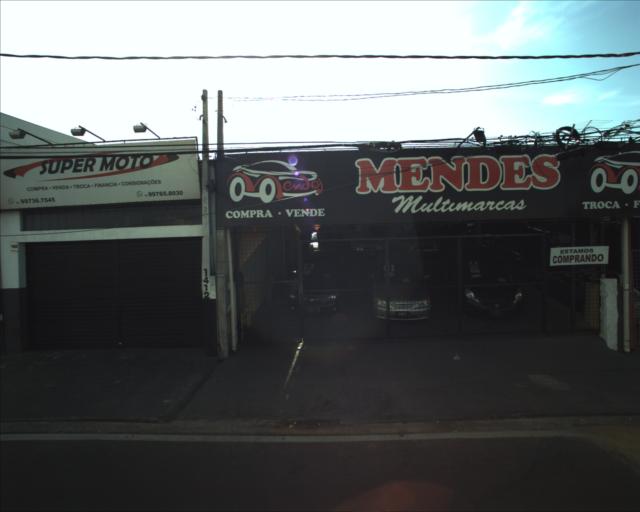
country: BR
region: Sao Paulo
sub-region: Sorocaba
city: Sorocaba
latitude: -23.4871
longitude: -47.4648
